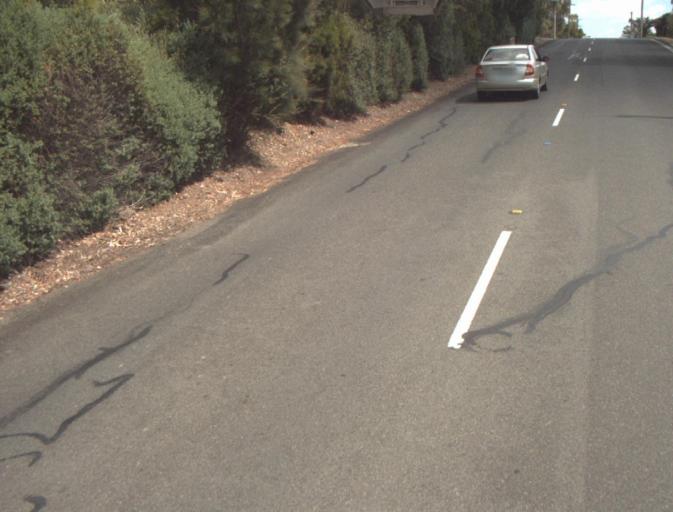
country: AU
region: Tasmania
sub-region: Launceston
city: Newstead
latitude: -41.4666
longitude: 147.1759
